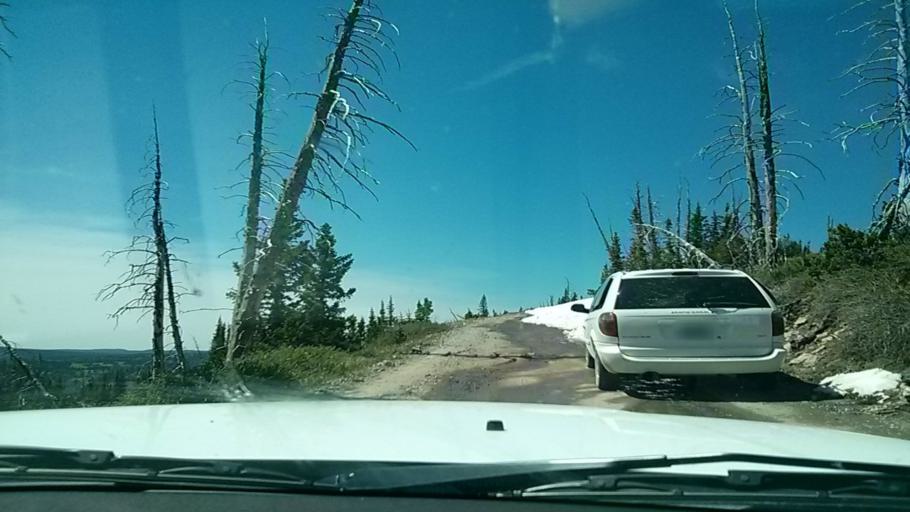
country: US
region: Utah
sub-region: Iron County
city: Parowan
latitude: 37.6855
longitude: -112.8221
